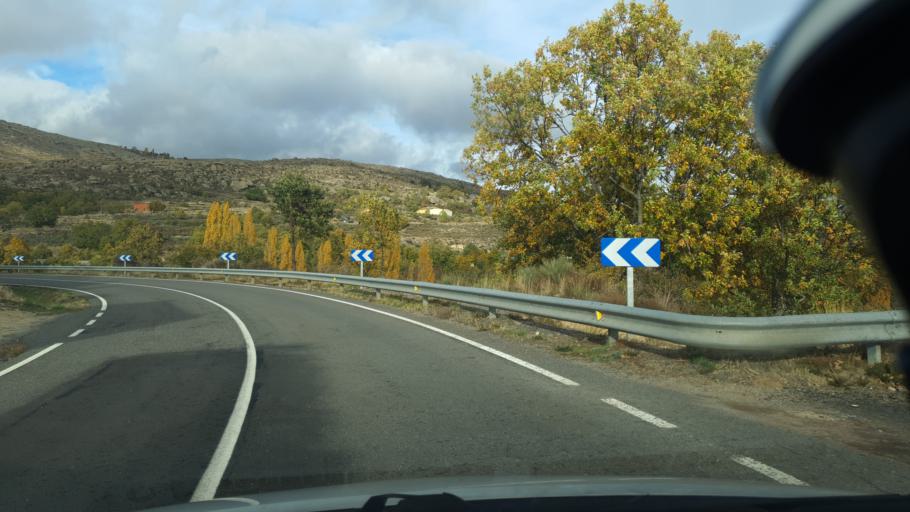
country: ES
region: Castille and Leon
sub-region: Provincia de Avila
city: Navalosa
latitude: 40.3965
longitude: -4.9405
